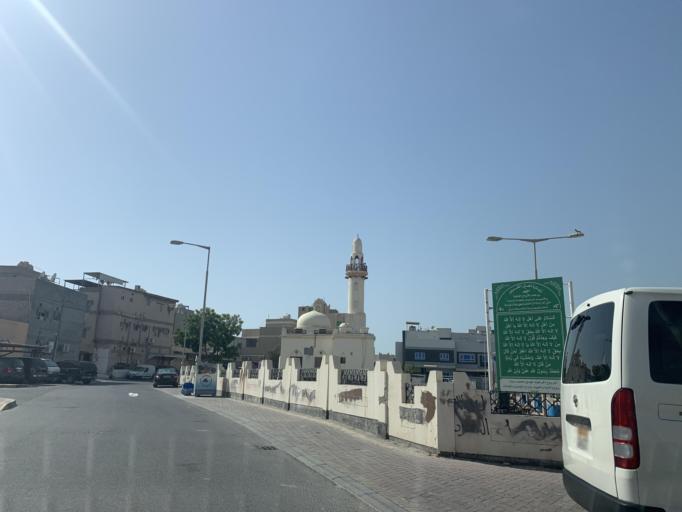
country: BH
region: Manama
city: Jidd Hafs
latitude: 26.2308
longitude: 50.4836
